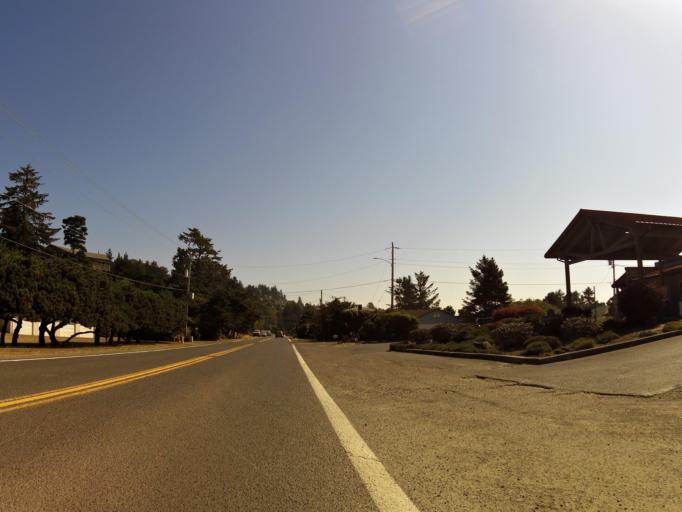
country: US
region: Oregon
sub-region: Tillamook County
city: Pacific City
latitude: 45.1984
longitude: -123.9603
